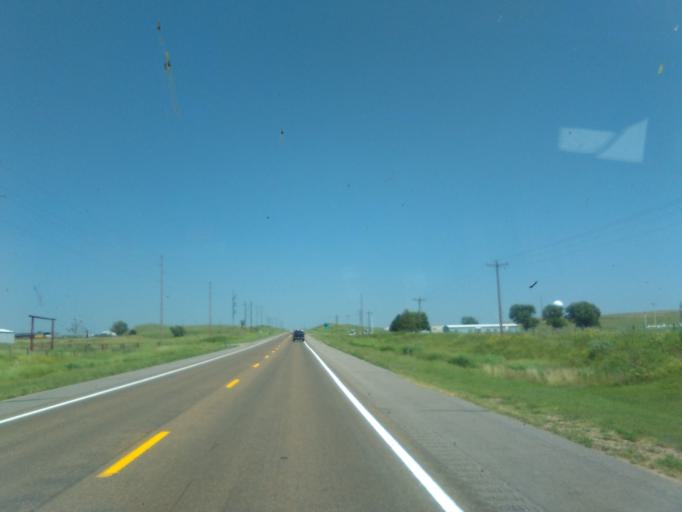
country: US
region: Nebraska
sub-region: Lincoln County
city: North Platte
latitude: 40.8221
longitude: -100.7537
